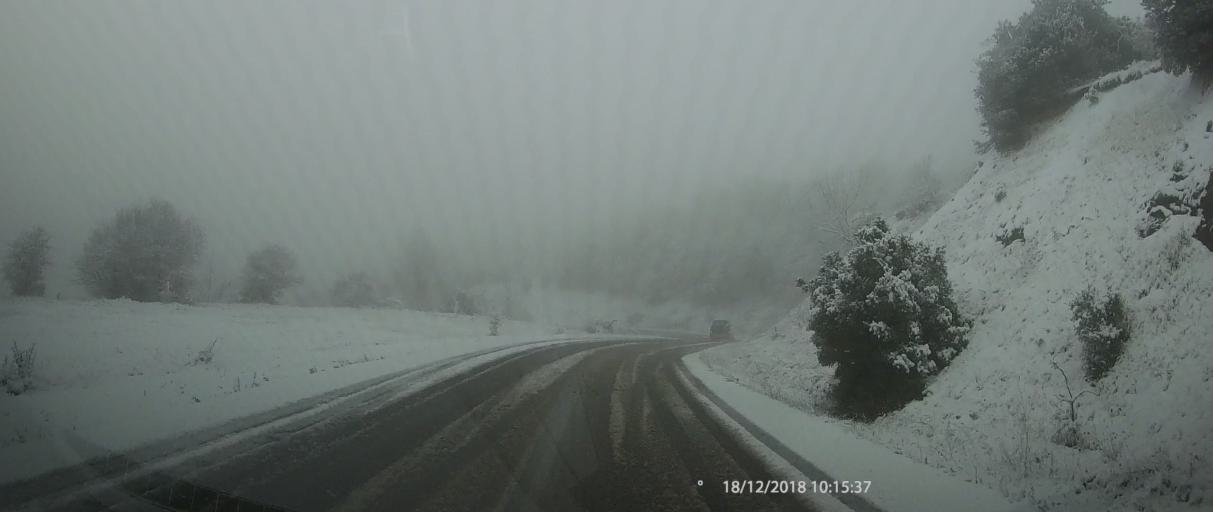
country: GR
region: Thessaly
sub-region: Nomos Larisis
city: Livadi
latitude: 40.1114
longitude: 22.2076
